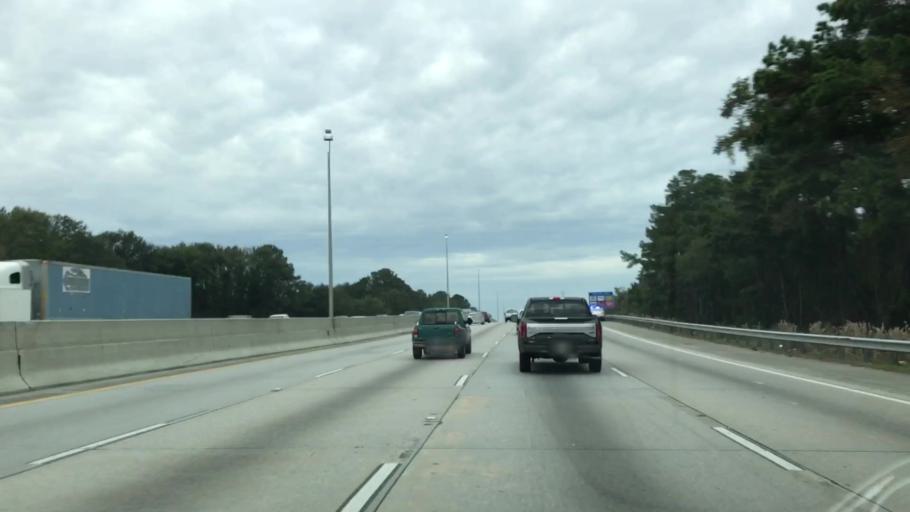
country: US
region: South Carolina
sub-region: Berkeley County
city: Hanahan
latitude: 32.9196
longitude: -80.0358
